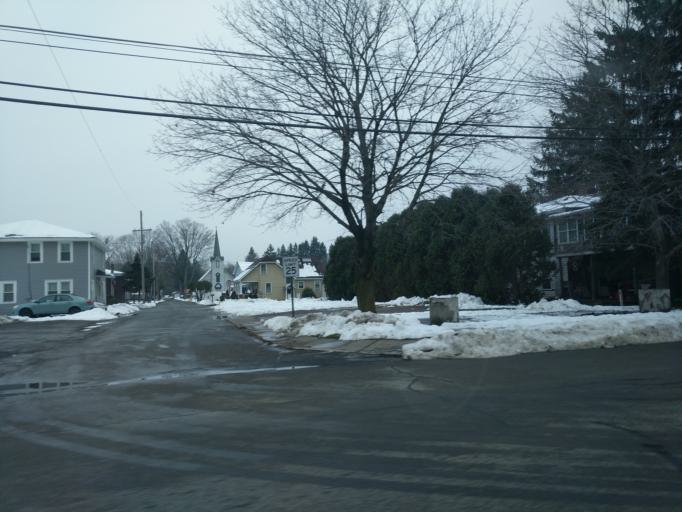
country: US
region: Pennsylvania
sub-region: Tioga County
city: Mansfield
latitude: 41.9093
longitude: -77.1333
